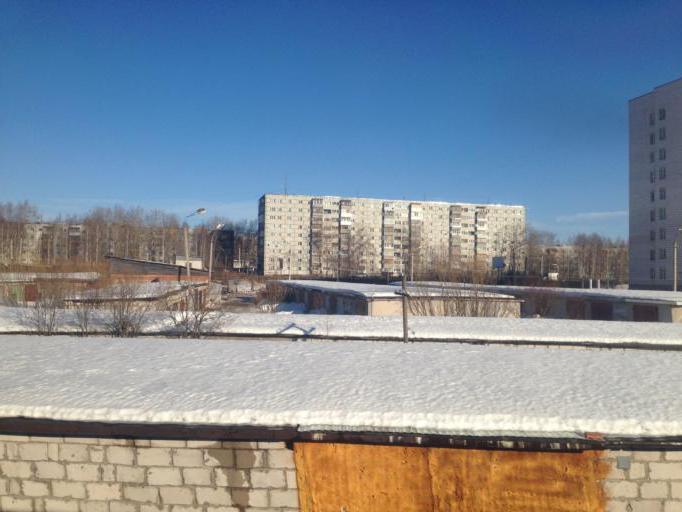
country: RU
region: Komi Republic
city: Ezhva
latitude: 61.7899
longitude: 50.7390
